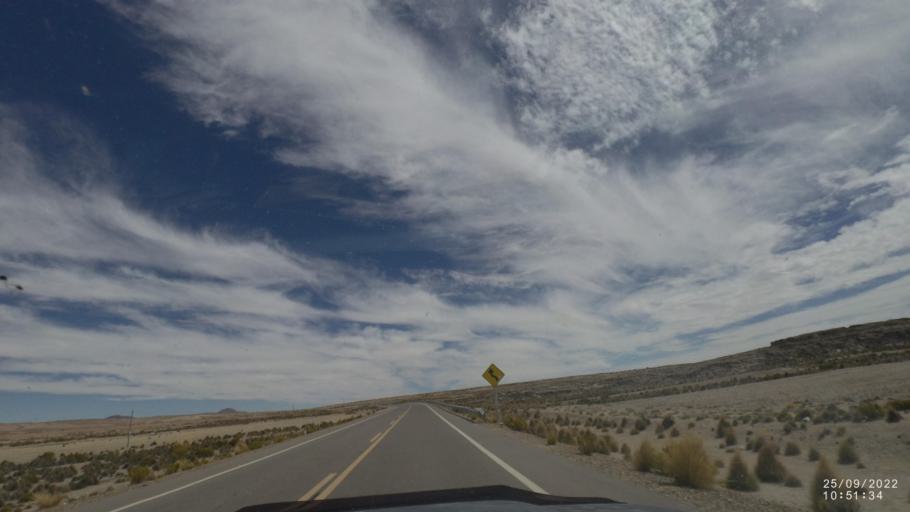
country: BO
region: Oruro
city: Challapata
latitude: -19.5608
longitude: -66.8498
